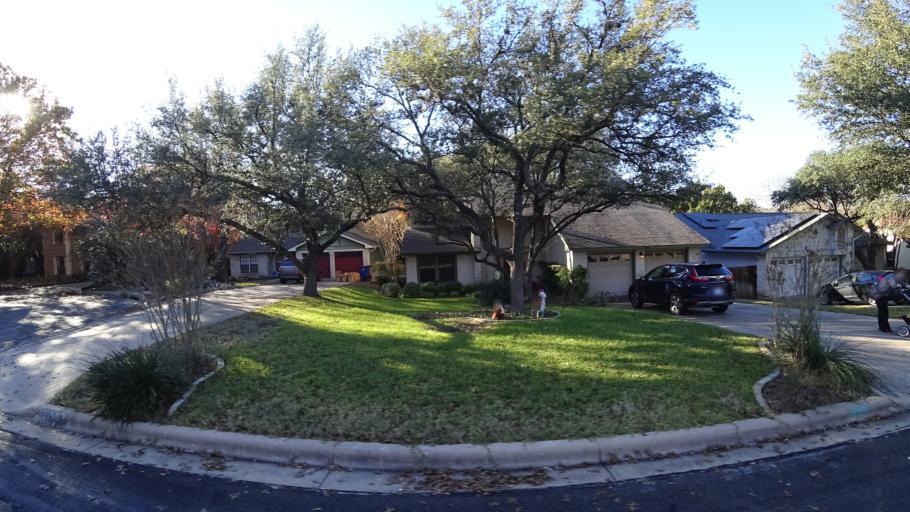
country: US
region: Texas
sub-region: Travis County
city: Wells Branch
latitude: 30.3990
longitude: -97.6980
